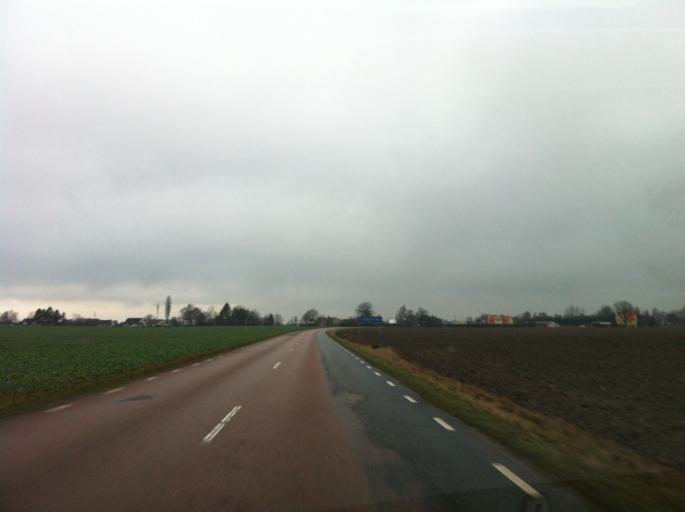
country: SE
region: Skane
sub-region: Helsingborg
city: Barslov
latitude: 55.9817
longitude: 12.8555
